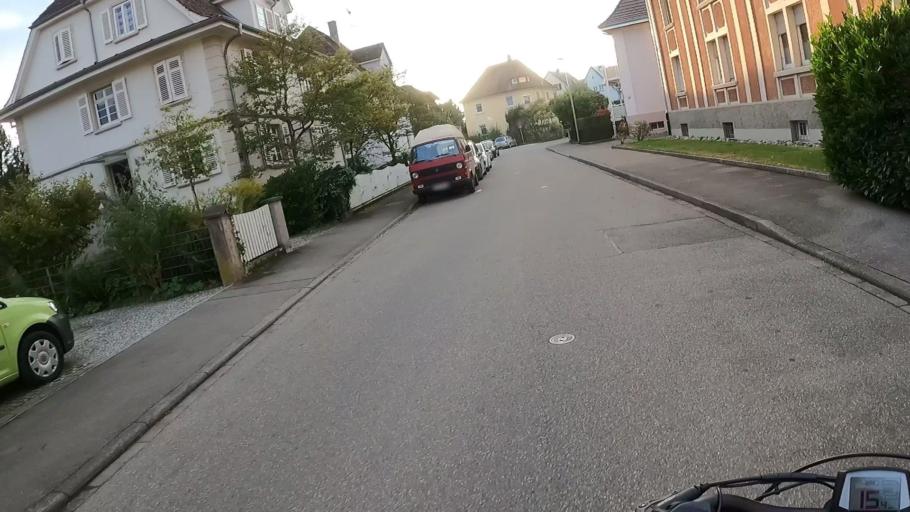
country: DE
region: Baden-Wuerttemberg
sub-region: Freiburg Region
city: Radolfzell am Bodensee
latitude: 47.7426
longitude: 8.9626
